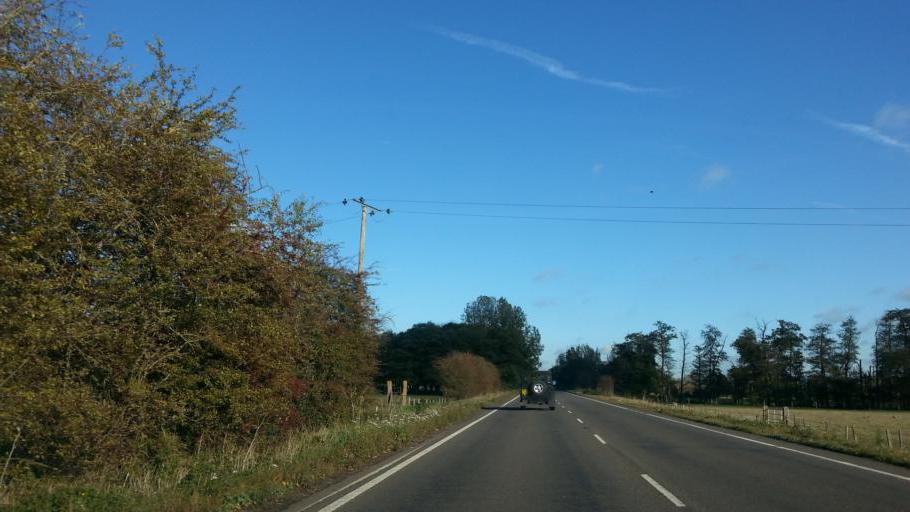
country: GB
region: England
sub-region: Suffolk
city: Bungay
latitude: 52.4329
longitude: 1.3759
